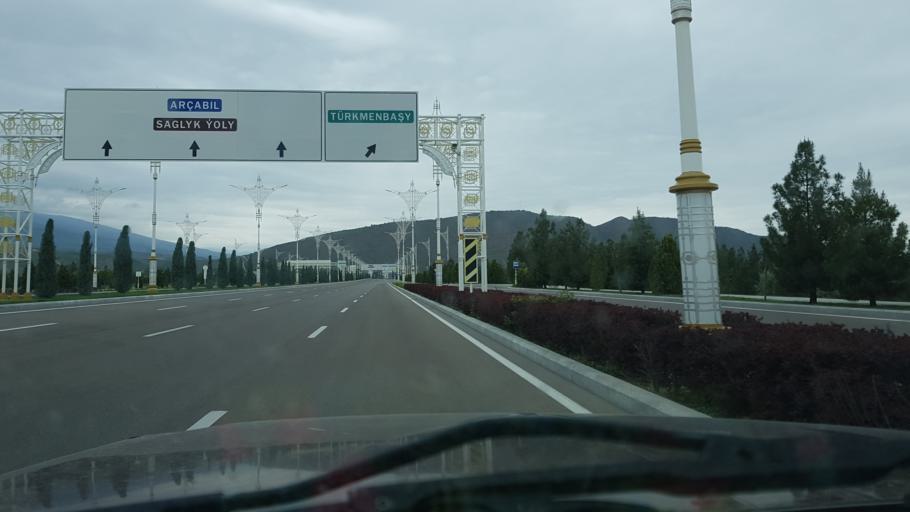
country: TM
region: Ahal
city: Ashgabat
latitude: 37.8963
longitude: 58.2634
